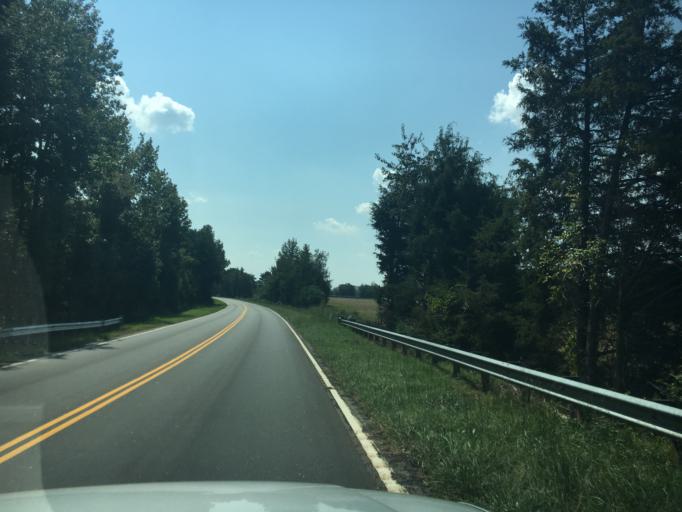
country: US
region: Georgia
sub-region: Hart County
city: Hartwell
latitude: 34.3890
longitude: -82.8097
